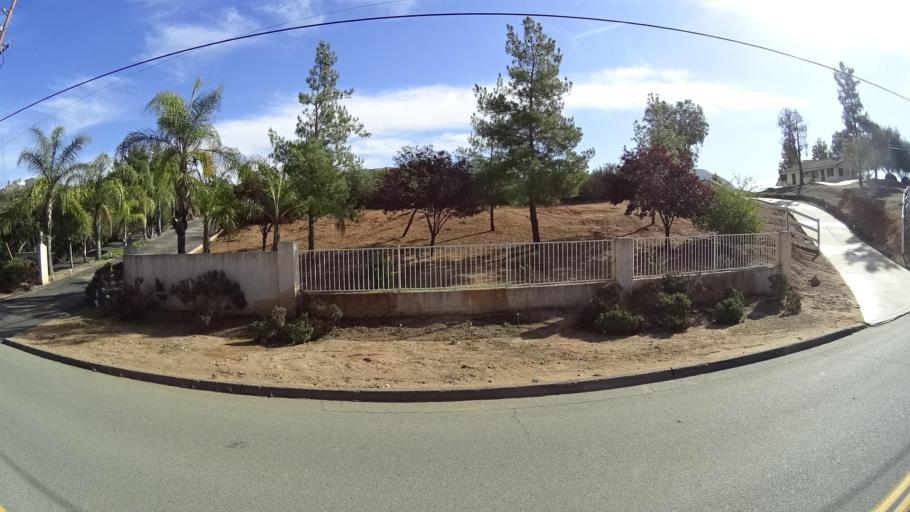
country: US
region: California
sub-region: San Diego County
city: Alpine
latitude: 32.8167
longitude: -116.7421
